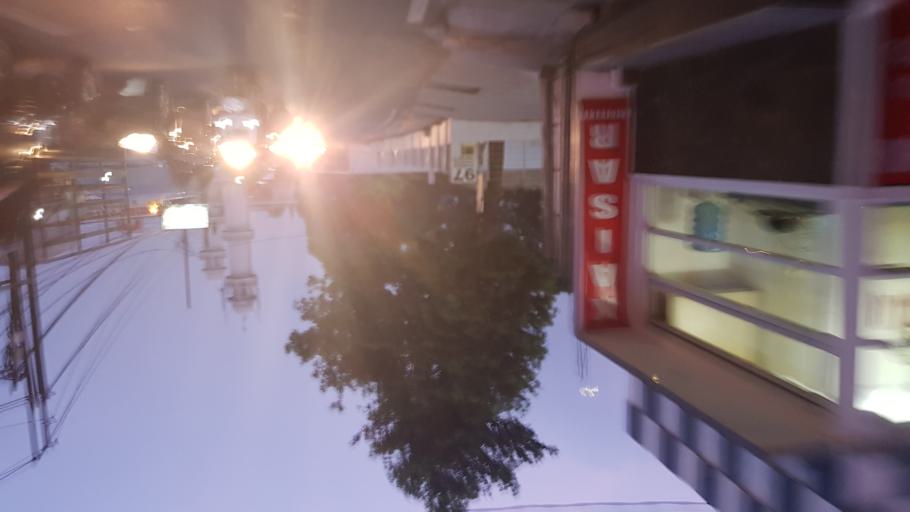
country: ID
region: West Java
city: Depok
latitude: -6.3465
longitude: 106.8028
